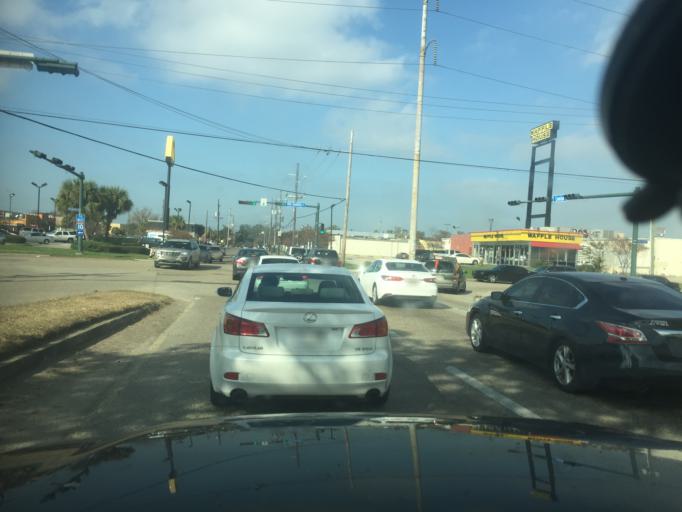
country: US
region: Louisiana
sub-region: Saint Bernard Parish
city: Arabi
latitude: 30.0037
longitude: -90.0355
